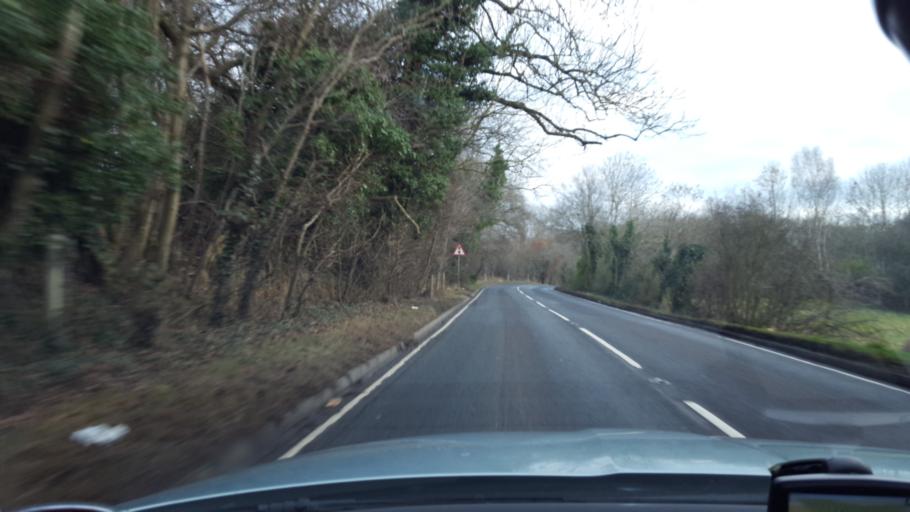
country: GB
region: Scotland
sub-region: West Lothian
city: Broxburn
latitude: 55.9771
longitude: -3.5069
